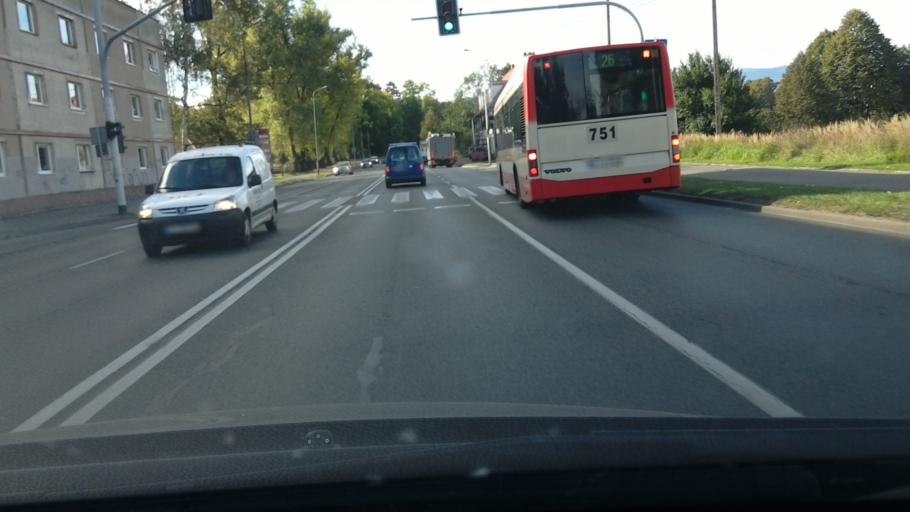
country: PL
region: Lower Silesian Voivodeship
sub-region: Jelenia Gora
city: Jelenia Gora
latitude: 50.8889
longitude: 15.7201
